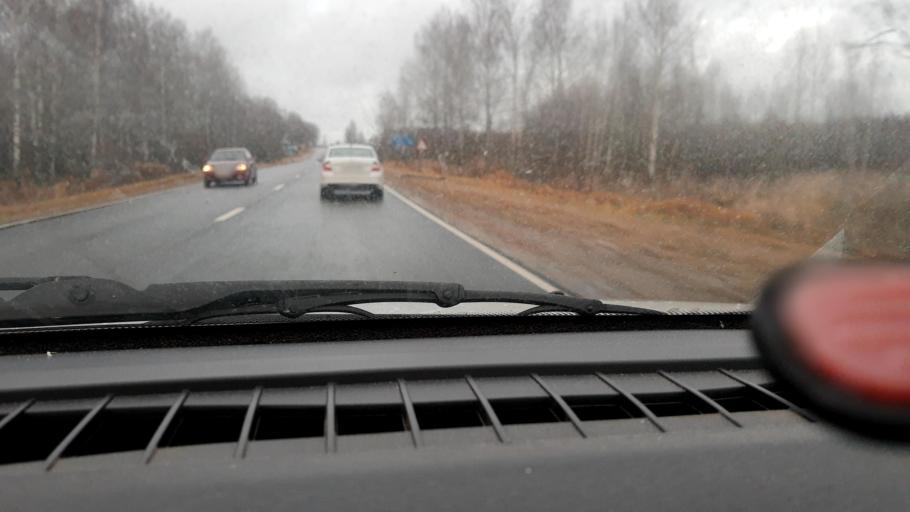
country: RU
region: Nizjnij Novgorod
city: Krasnyye Baki
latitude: 57.0917
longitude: 45.1491
